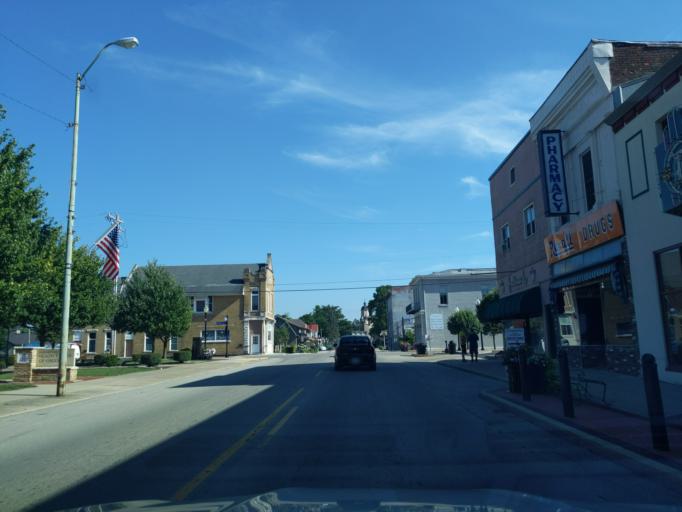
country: US
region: Indiana
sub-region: Ripley County
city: Osgood
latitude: 39.1298
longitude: -85.2916
